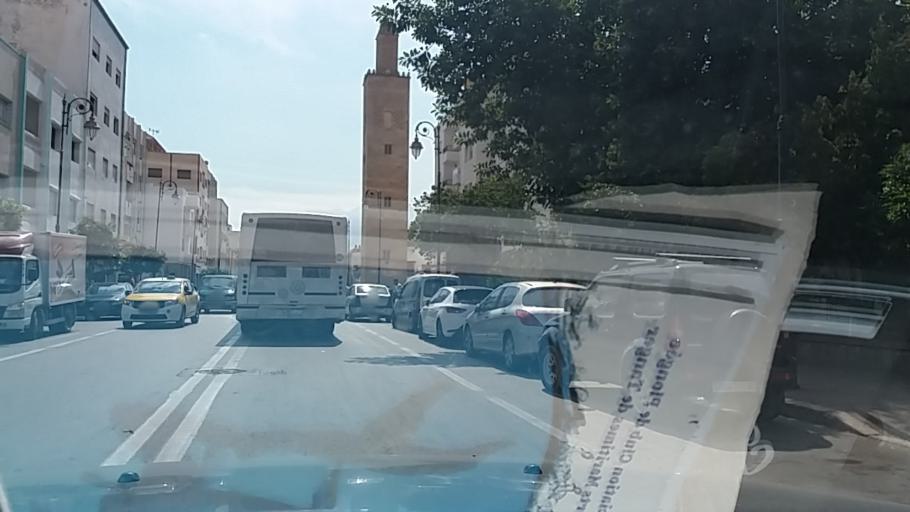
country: MA
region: Tanger-Tetouan
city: Tetouan
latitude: 35.5821
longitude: -5.3454
